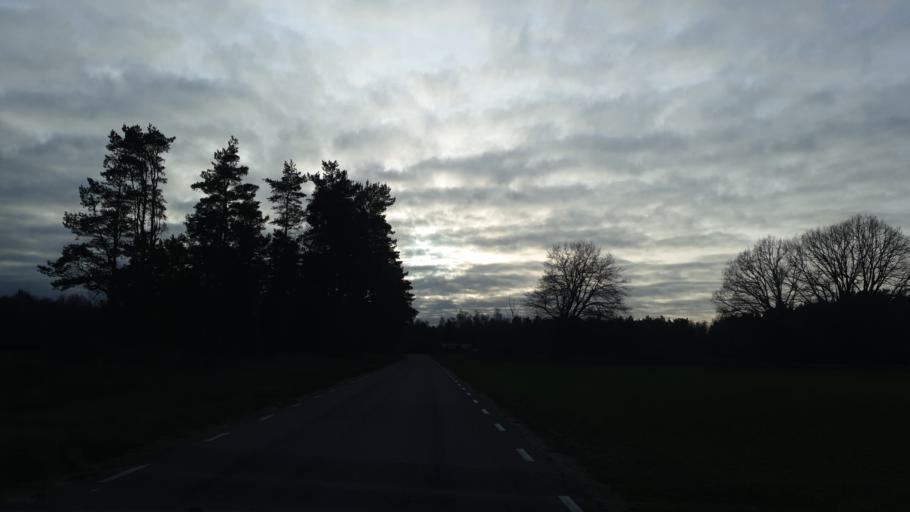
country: SE
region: Kalmar
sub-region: Torsas Kommun
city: Torsas
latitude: 56.3136
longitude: 16.0351
